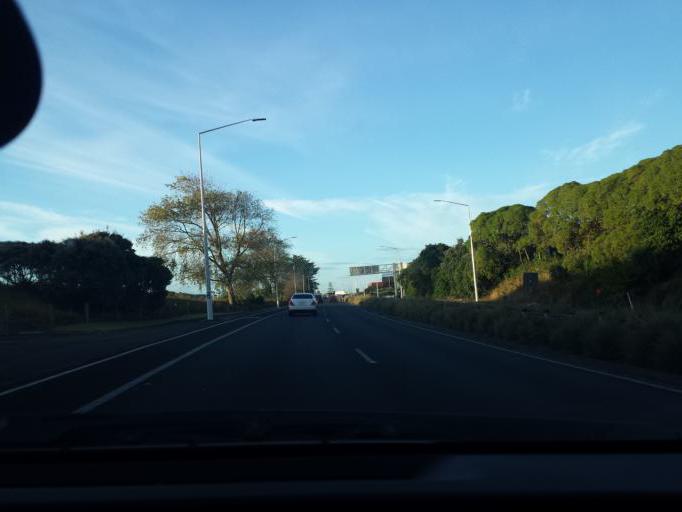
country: NZ
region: Auckland
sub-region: Auckland
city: Mangere
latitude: -36.9858
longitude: 174.7855
